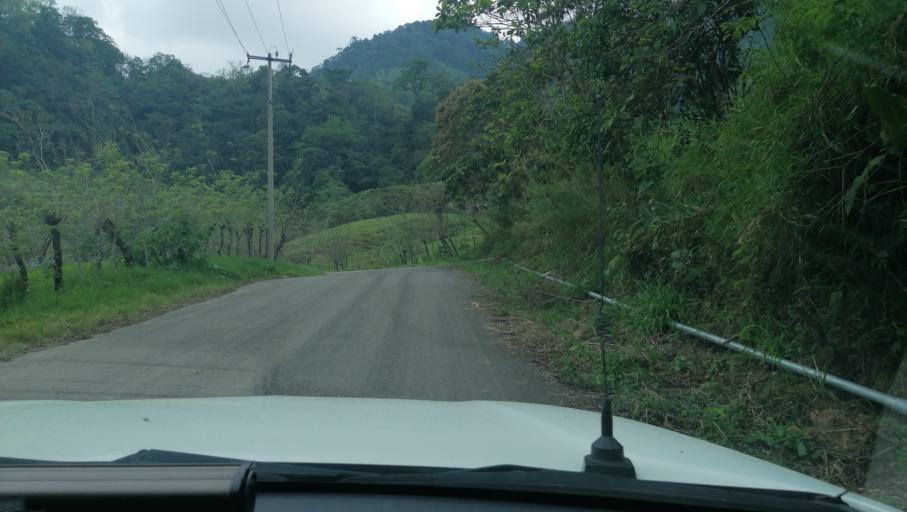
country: MX
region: Chiapas
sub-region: Francisco Leon
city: San Miguel la Sardina
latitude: 17.2767
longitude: -93.2717
